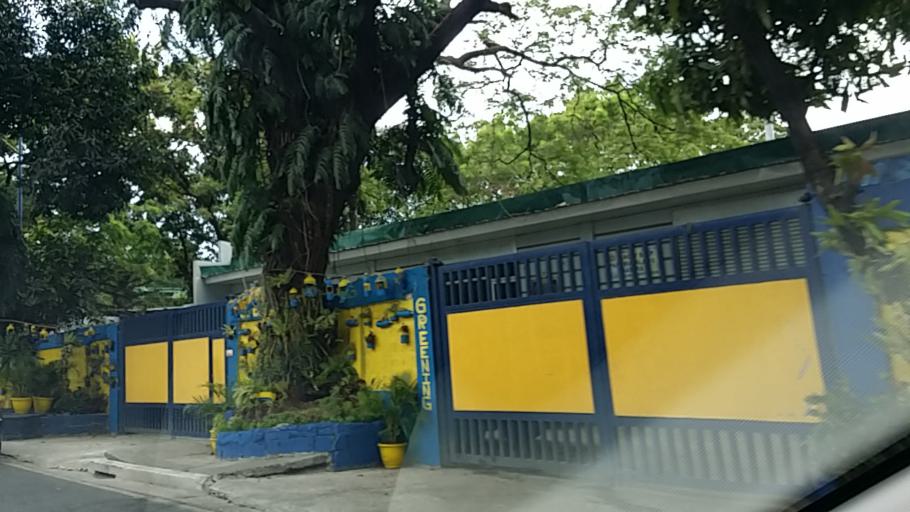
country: PH
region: Metro Manila
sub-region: Mandaluyong
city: Mandaluyong City
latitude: 14.5807
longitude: 121.0443
